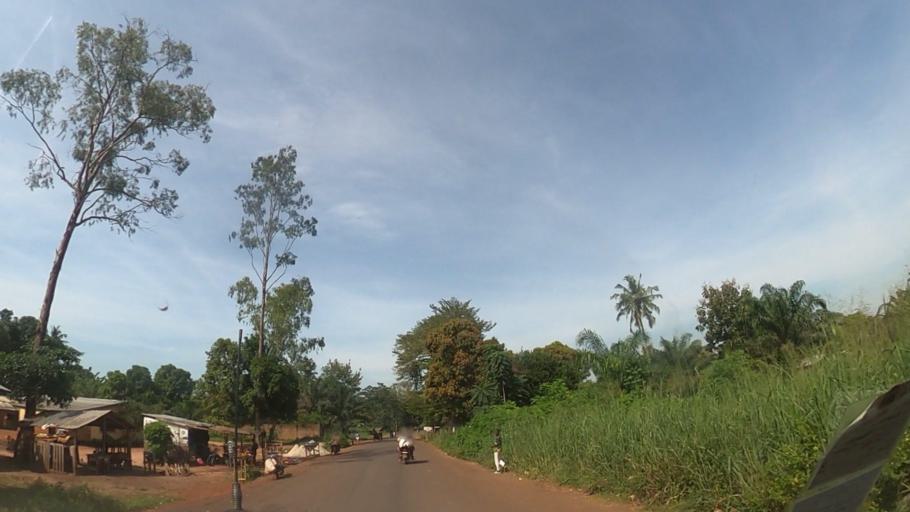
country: CF
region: Bangui
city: Bangui
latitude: 4.3119
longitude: 18.4848
